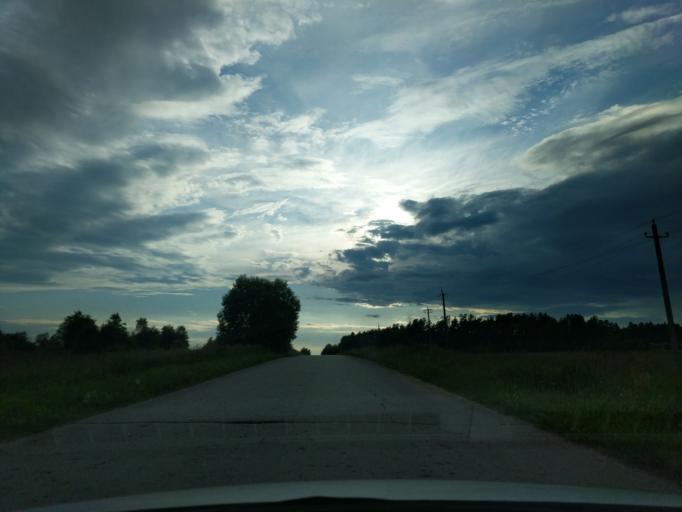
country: RU
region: Kaluga
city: Myatlevo
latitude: 54.8275
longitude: 35.6627
